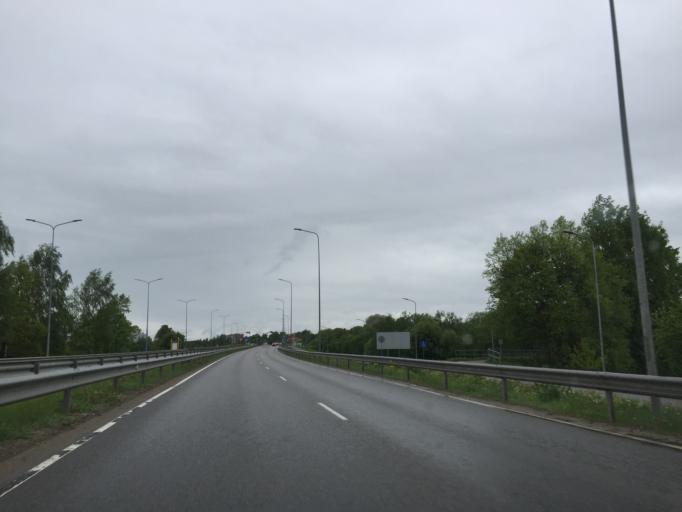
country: LV
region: Ogre
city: Ogre
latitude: 56.8071
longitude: 24.6059
